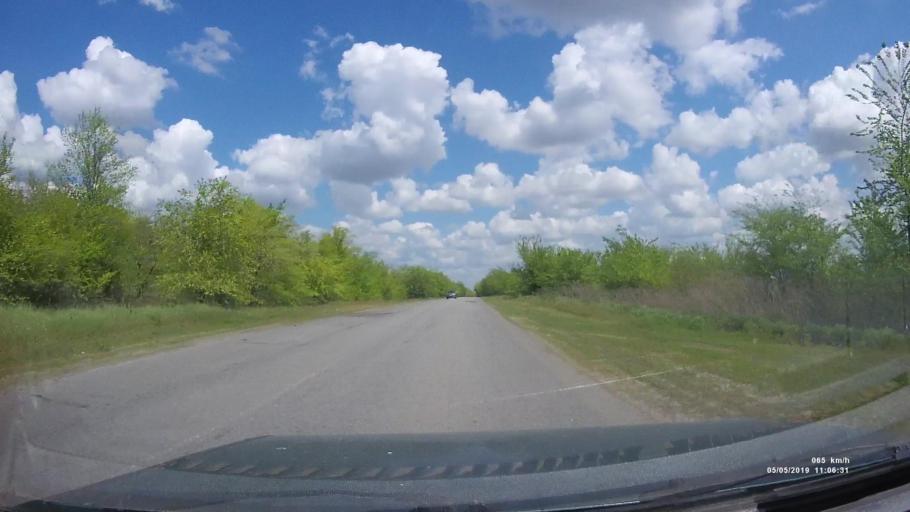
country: RU
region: Rostov
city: Ust'-Donetskiy
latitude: 47.7162
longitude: 40.9110
